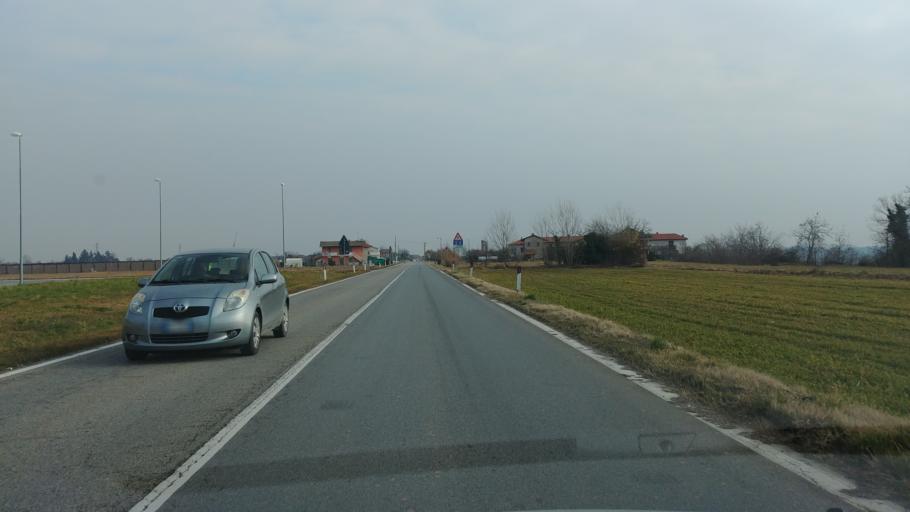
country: IT
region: Piedmont
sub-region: Provincia di Cuneo
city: Cuneo
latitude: 44.4289
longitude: 7.5757
